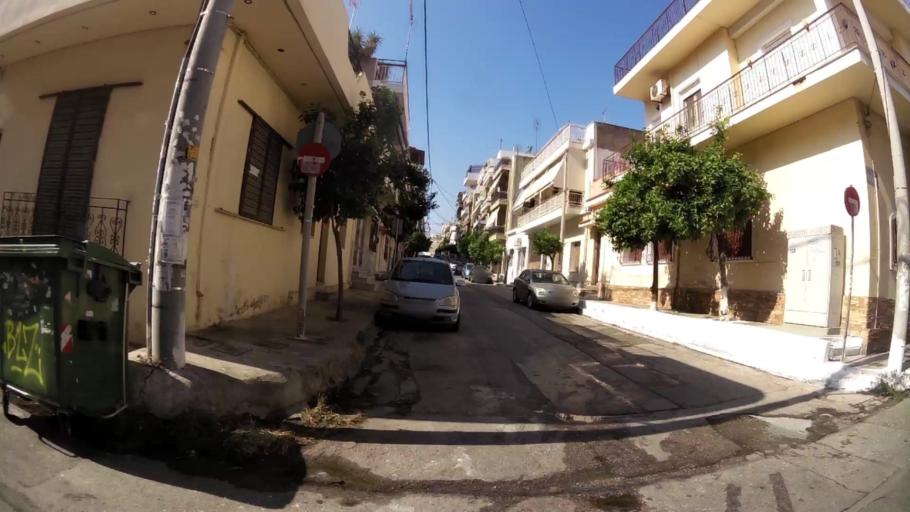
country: GR
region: Attica
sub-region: Nomos Piraios
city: Keratsini
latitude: 37.9619
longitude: 23.6285
